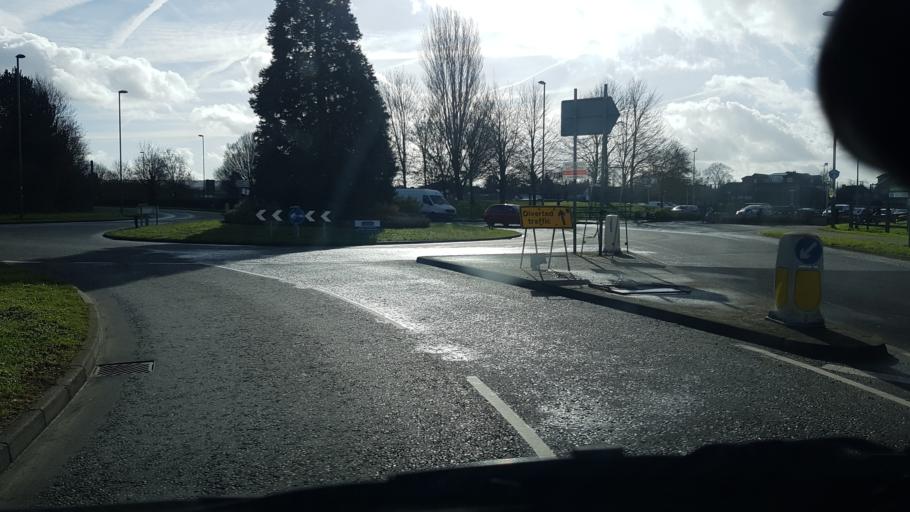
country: GB
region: England
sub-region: Surrey
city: Send
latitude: 51.2622
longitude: -0.5478
